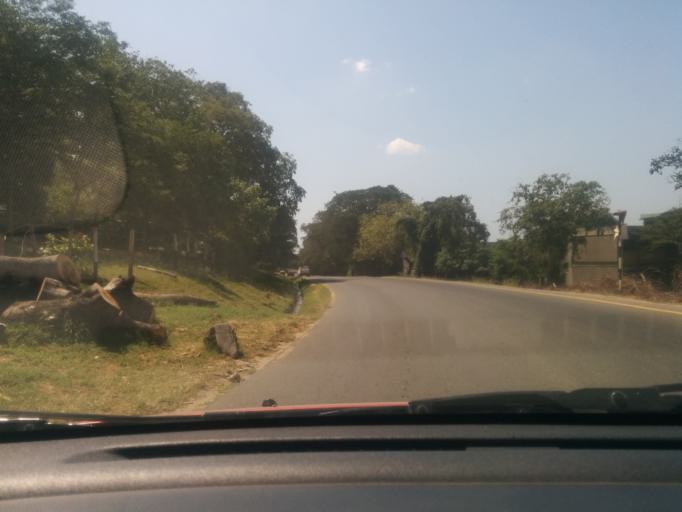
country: TZ
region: Dar es Salaam
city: Magomeni
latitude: -6.7783
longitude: 39.2072
